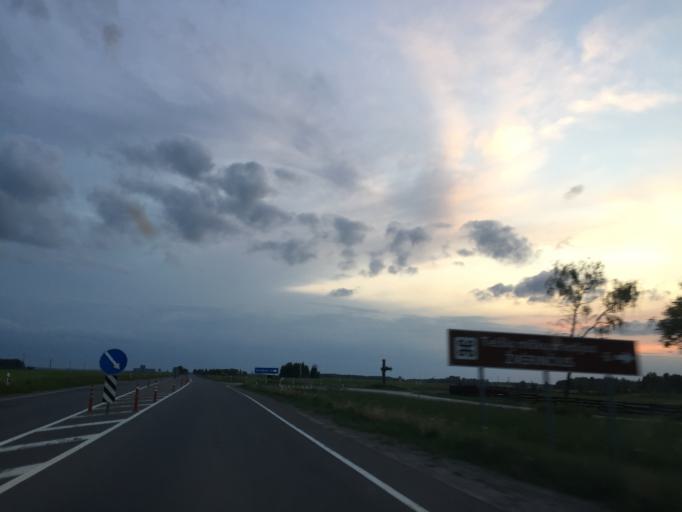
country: LT
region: Telsiu apskritis
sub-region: Telsiai
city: Telsiai
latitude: 56.0025
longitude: 22.4360
